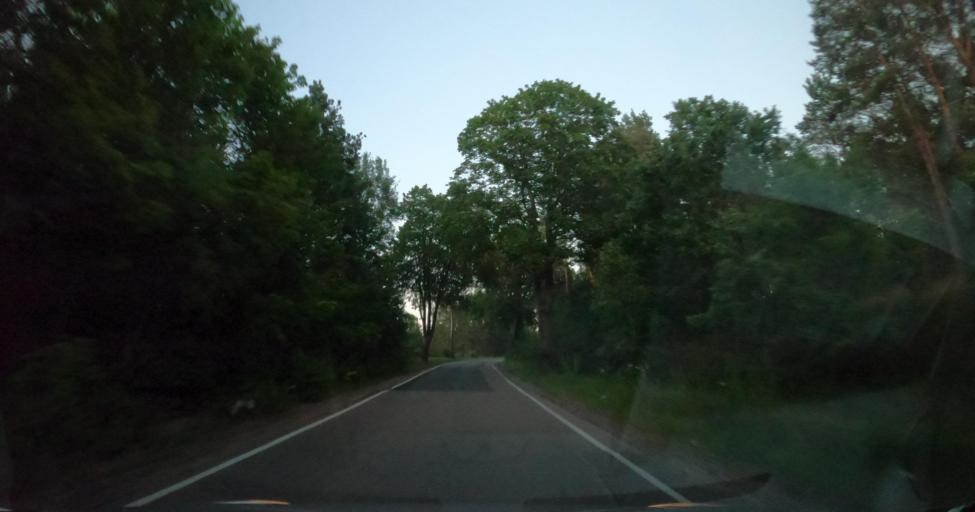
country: PL
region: Pomeranian Voivodeship
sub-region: Powiat wejherowski
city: Luzino
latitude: 54.4662
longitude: 18.1041
